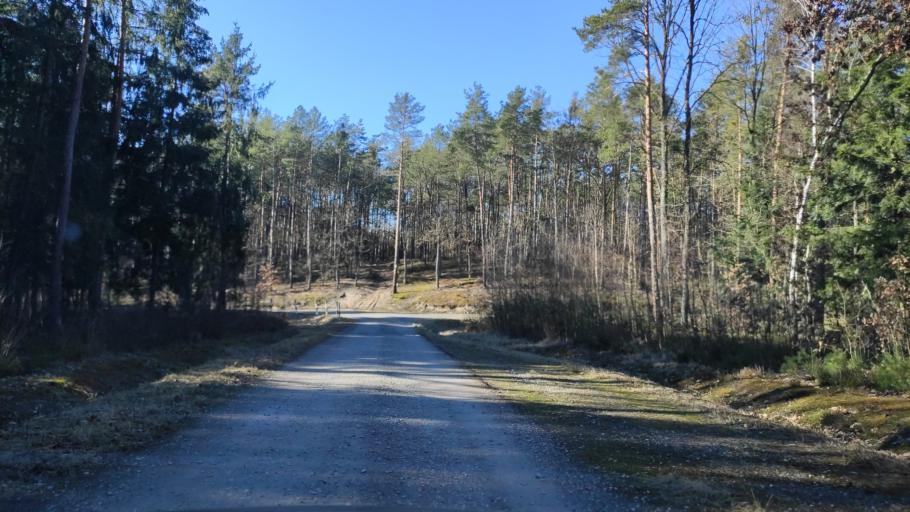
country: PL
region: Masovian Voivodeship
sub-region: Powiat radomski
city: Jedlnia-Letnisko
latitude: 51.4738
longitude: 21.2967
